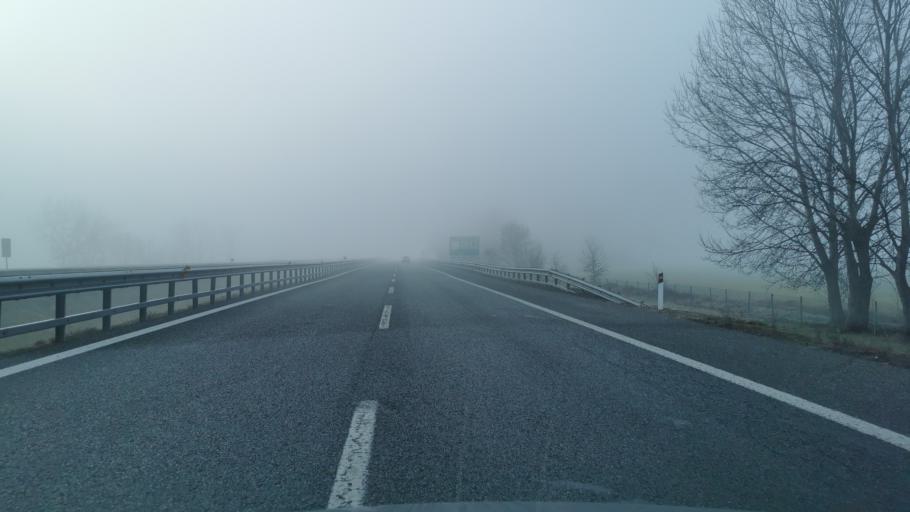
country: IT
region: Piedmont
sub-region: Provincia di Cuneo
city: Marene
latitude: 44.7111
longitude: 7.7611
